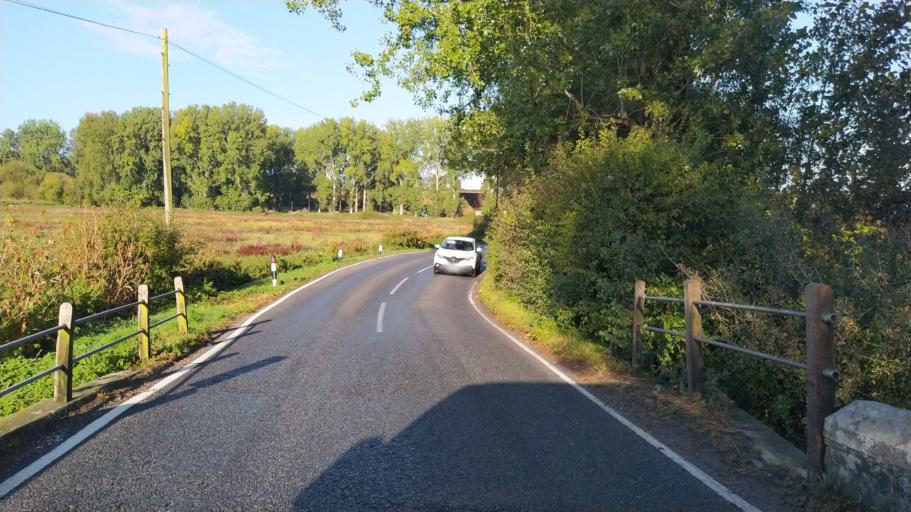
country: GB
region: England
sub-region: Dorset
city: Wimborne Minster
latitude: 50.8794
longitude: -1.9818
